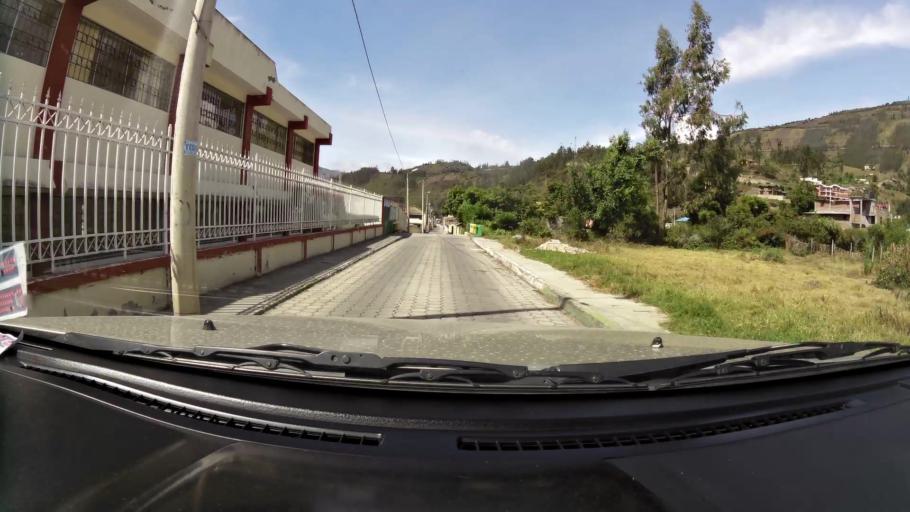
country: EC
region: Chimborazo
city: Guano
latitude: -1.5685
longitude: -78.5309
